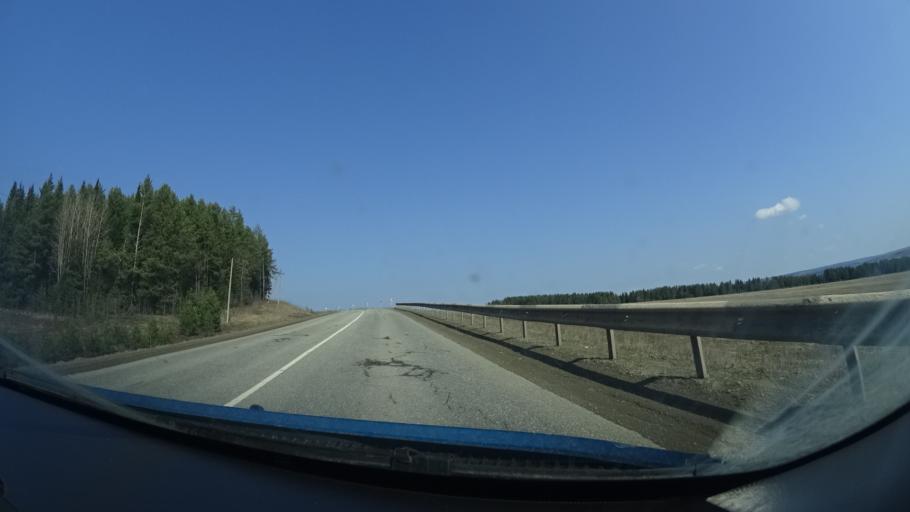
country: RU
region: Perm
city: Osa
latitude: 57.3136
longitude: 55.6224
